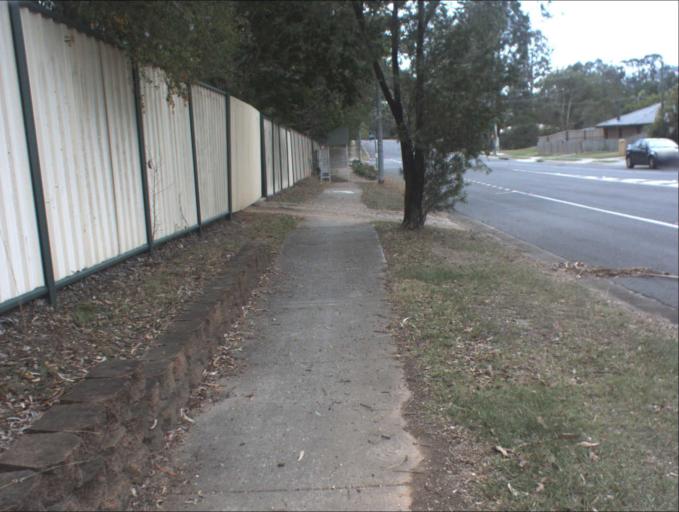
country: AU
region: Queensland
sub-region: Logan
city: Slacks Creek
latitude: -27.6758
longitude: 153.1812
